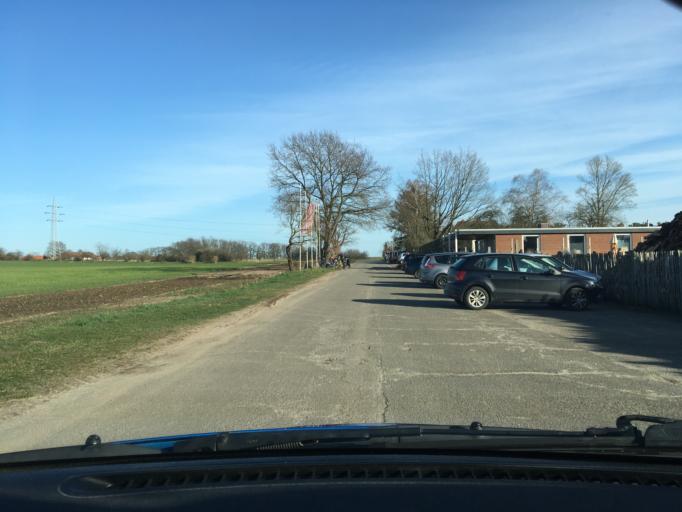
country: DE
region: Lower Saxony
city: Embsen
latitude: 53.2141
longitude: 10.3595
